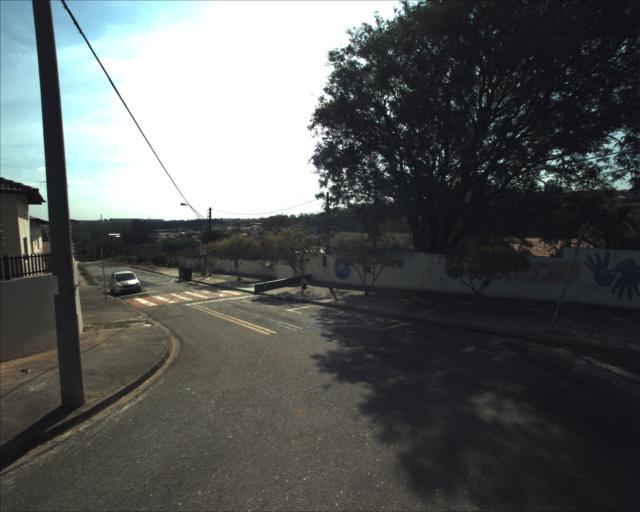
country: BR
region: Sao Paulo
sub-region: Sorocaba
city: Sorocaba
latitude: -23.4673
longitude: -47.4371
